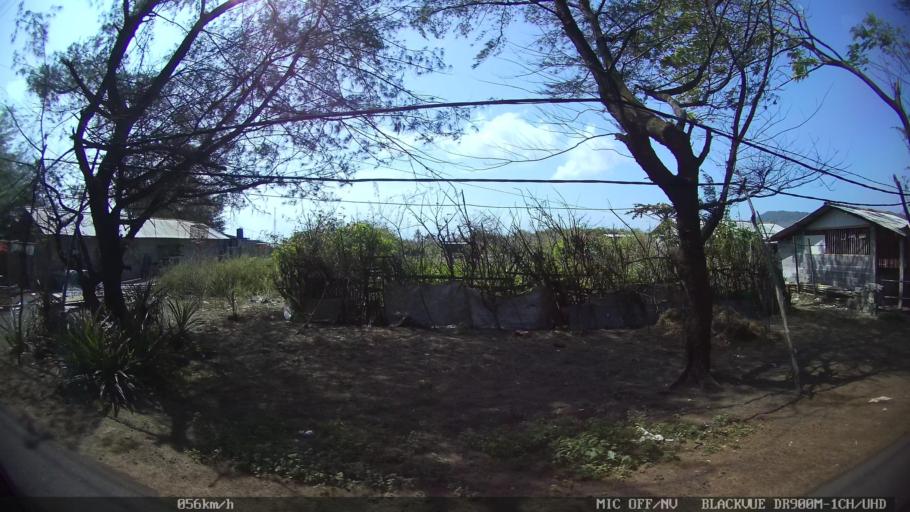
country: ID
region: Daerah Istimewa Yogyakarta
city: Bambanglipuro
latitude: -8.0142
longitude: 110.2979
